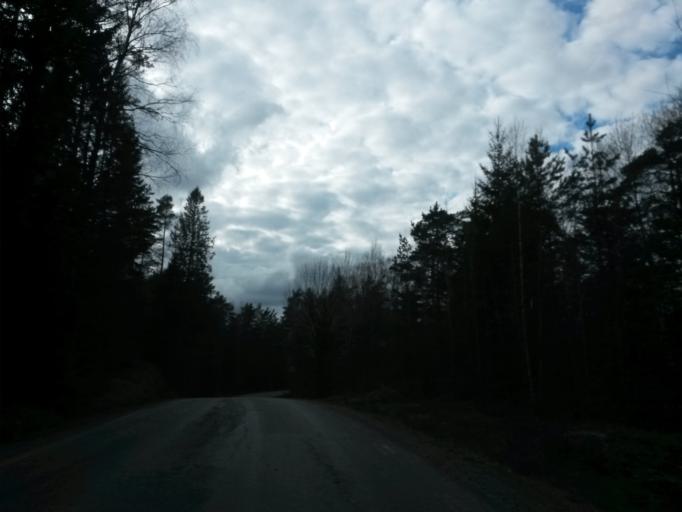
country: SE
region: Vaestra Goetaland
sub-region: Vargarda Kommun
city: Jonstorp
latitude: 57.9464
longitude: 12.6650
